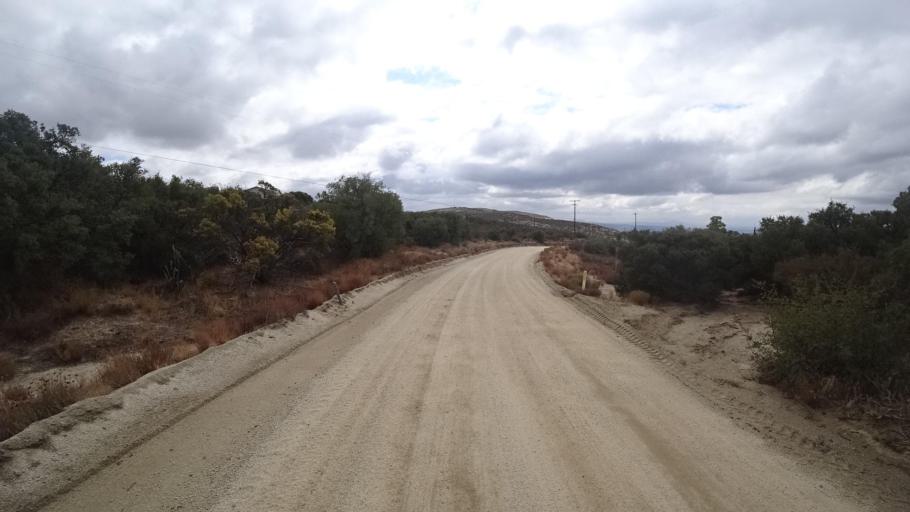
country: US
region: California
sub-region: San Diego County
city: Campo
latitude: 32.7066
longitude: -116.3884
